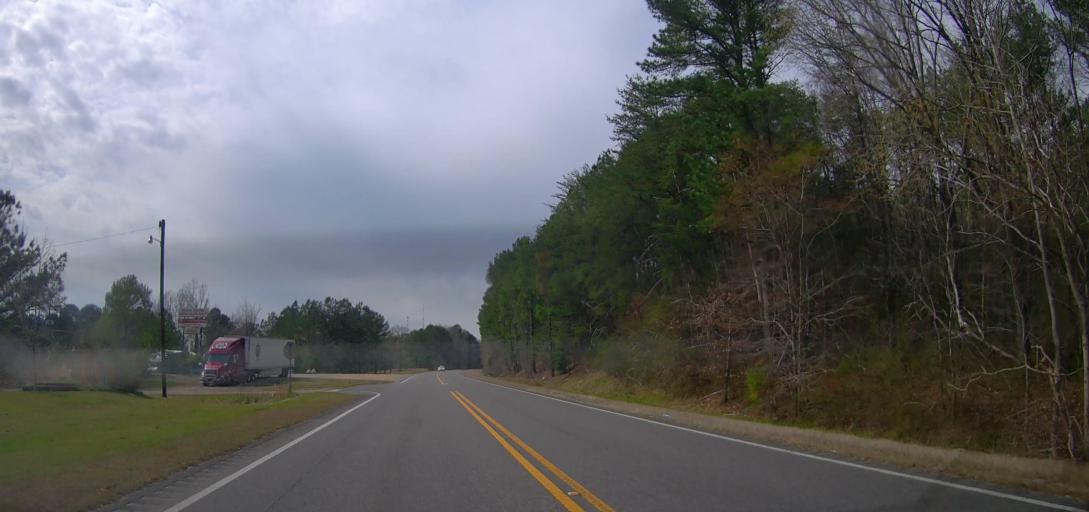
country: US
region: Alabama
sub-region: Walker County
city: Carbon Hill
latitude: 33.9015
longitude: -87.5460
